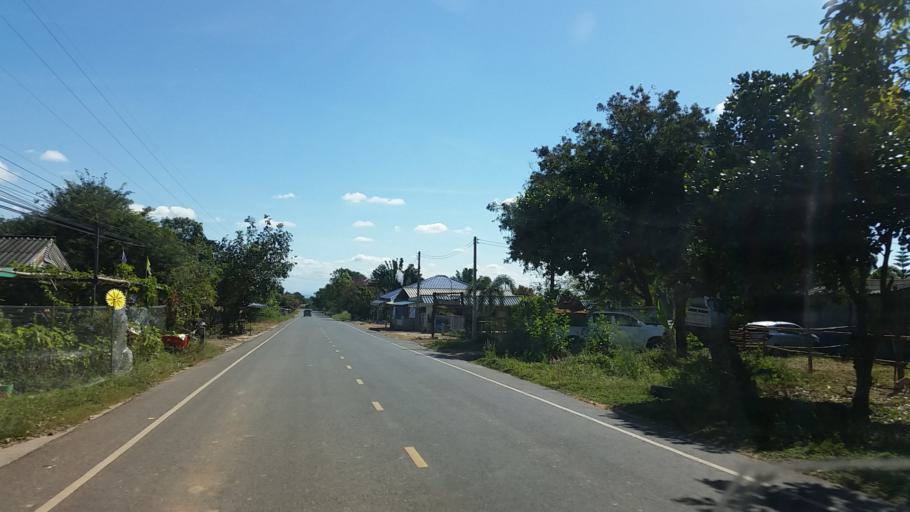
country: TH
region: Chaiyaphum
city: Sap Yai
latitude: 15.6144
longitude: 101.4023
